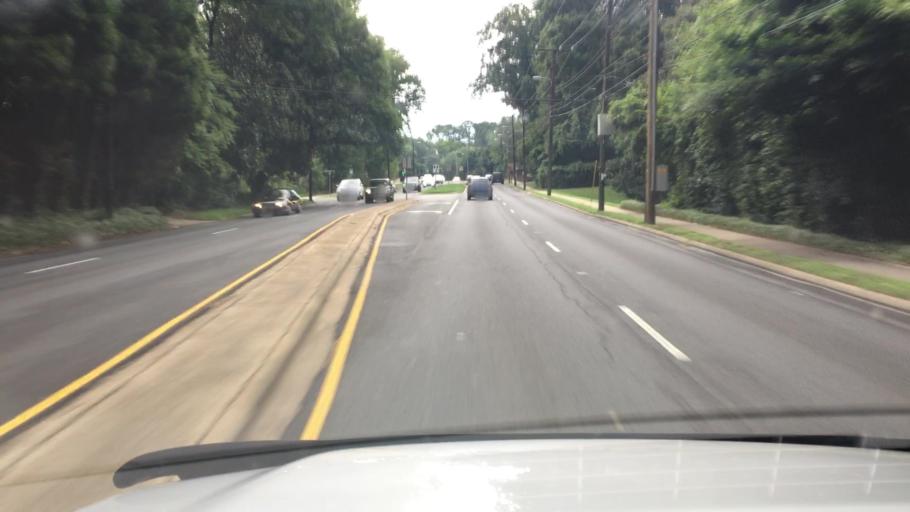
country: US
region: North Carolina
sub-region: Mecklenburg County
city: Charlotte
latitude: 35.1799
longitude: -80.8189
